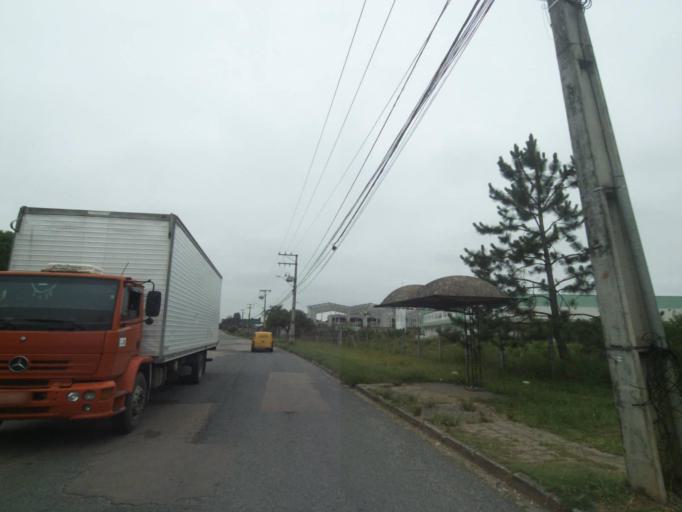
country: BR
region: Parana
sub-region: Araucaria
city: Araucaria
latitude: -25.5393
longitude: -49.3285
